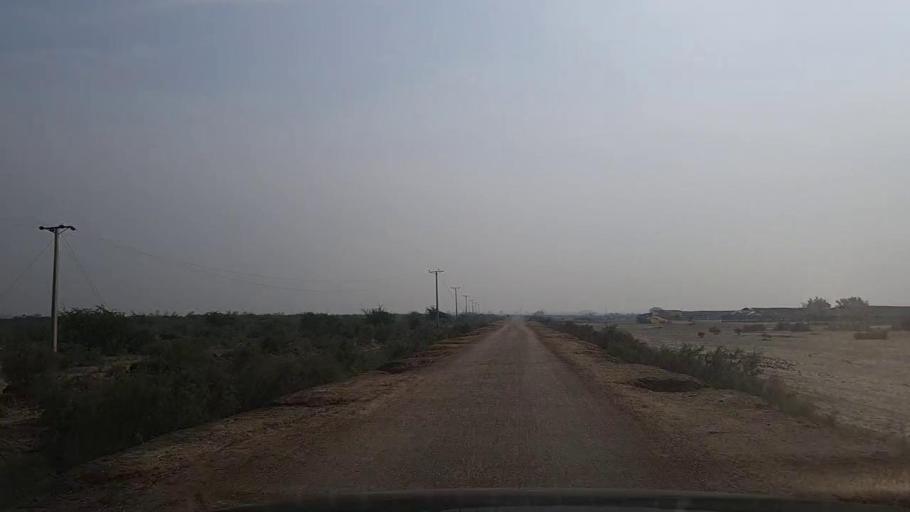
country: PK
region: Sindh
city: Mirpur Sakro
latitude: 24.3905
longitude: 67.7518
